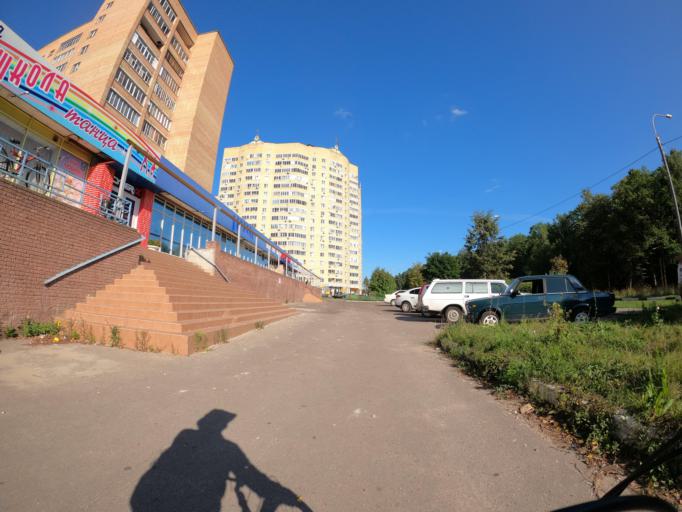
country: RU
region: Moskovskaya
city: Stupino
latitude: 54.8793
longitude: 38.0661
